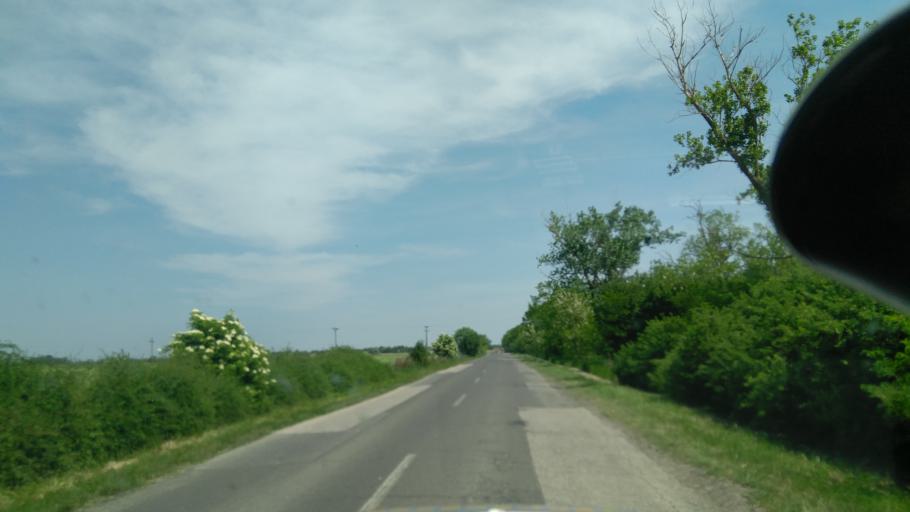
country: HU
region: Csongrad
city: Szekkutas
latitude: 46.5686
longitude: 20.5752
